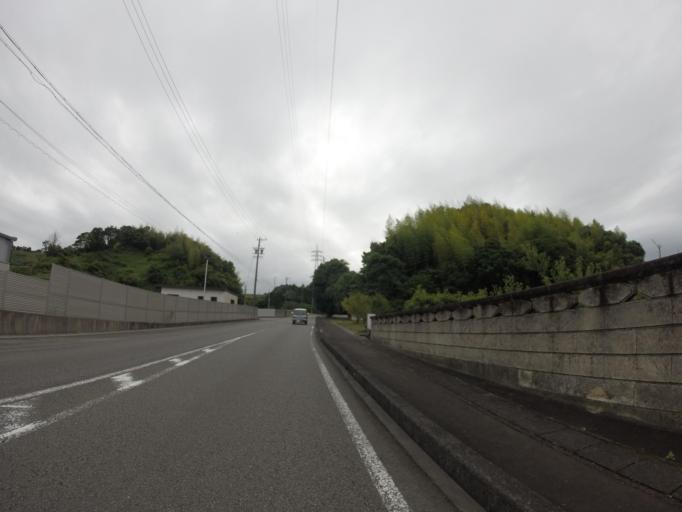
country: JP
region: Shizuoka
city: Sagara
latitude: 34.7297
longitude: 138.1808
